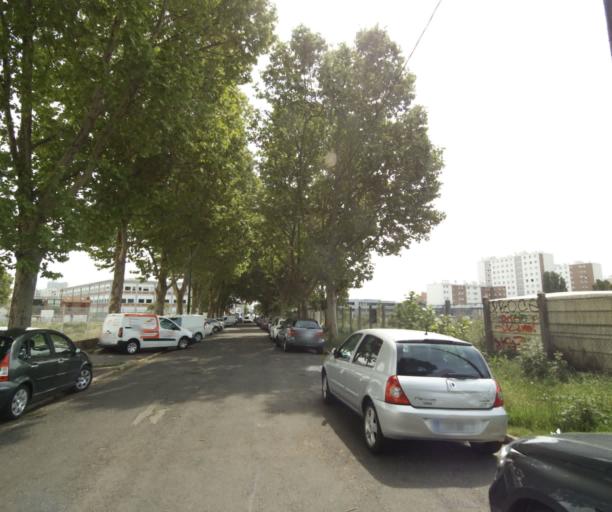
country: FR
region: Ile-de-France
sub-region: Departement des Hauts-de-Seine
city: Colombes
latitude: 48.9329
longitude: 2.2535
